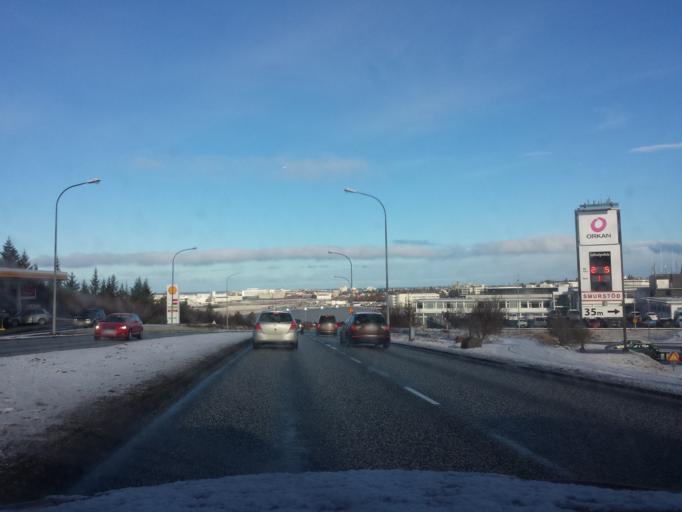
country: IS
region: Capital Region
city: Kopavogur
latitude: 64.1313
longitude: -21.9171
